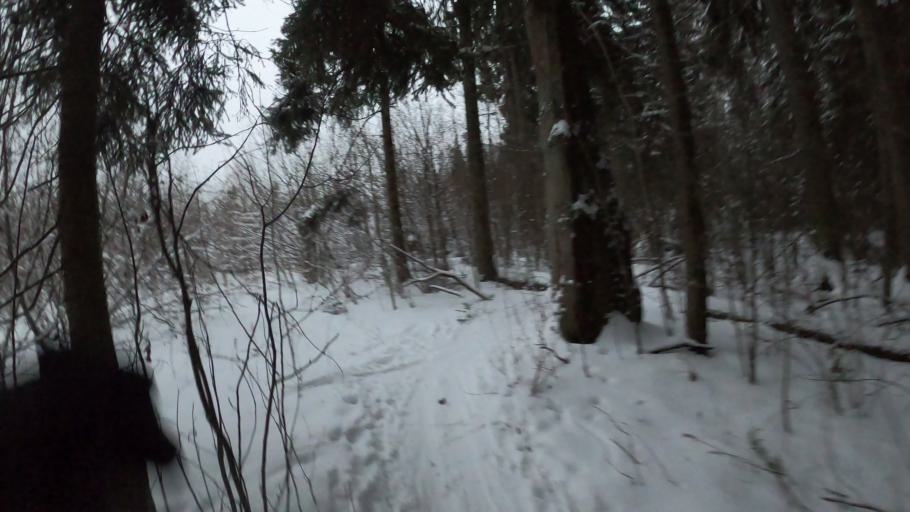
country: RU
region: Moskovskaya
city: Nakhabino
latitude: 55.8947
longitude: 37.2080
